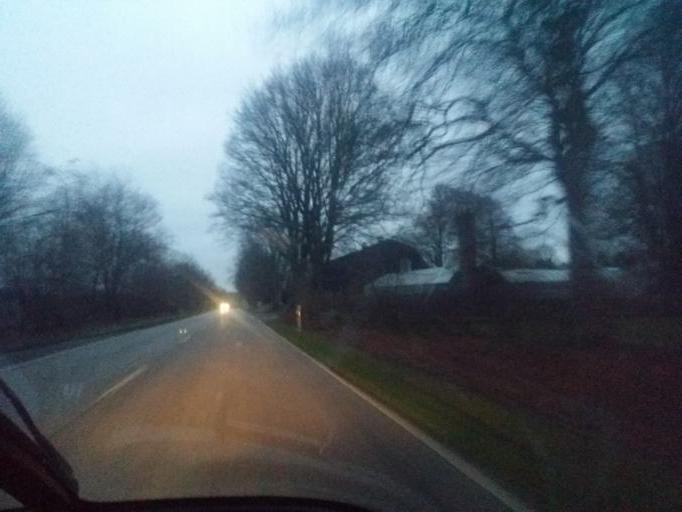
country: DE
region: Schleswig-Holstein
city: Warringholz
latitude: 54.0723
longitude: 9.4669
